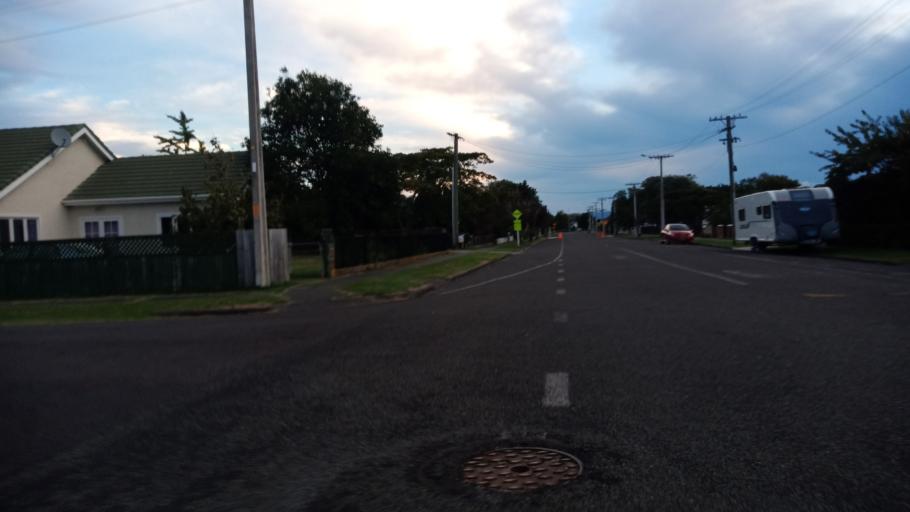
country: NZ
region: Gisborne
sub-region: Gisborne District
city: Gisborne
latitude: -38.6501
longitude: 178.0023
